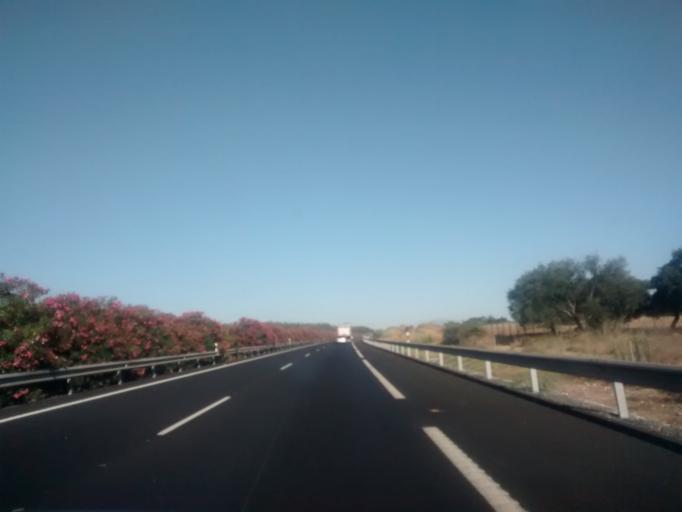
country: ES
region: Andalusia
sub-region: Provincia de Huelva
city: Villalba del Alcor
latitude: 37.3505
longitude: -6.4792
